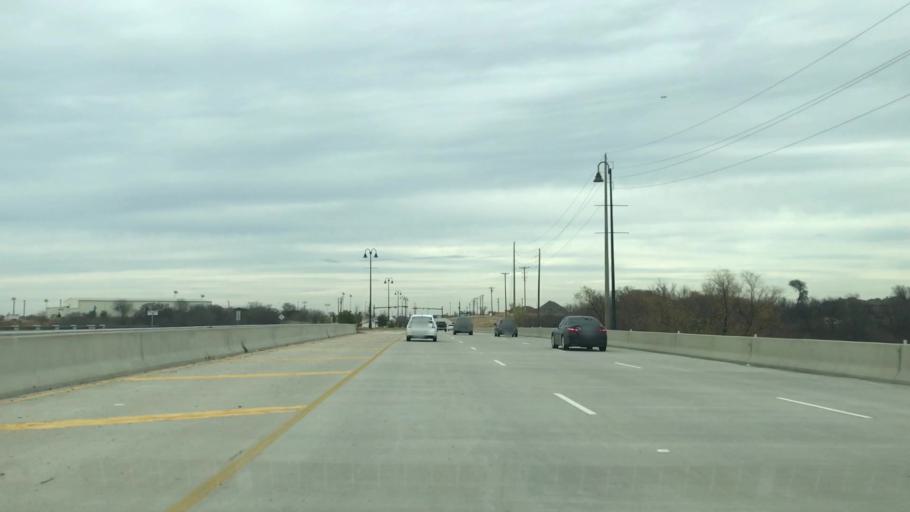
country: US
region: Texas
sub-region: Denton County
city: The Colony
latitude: 33.1096
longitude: -96.8917
